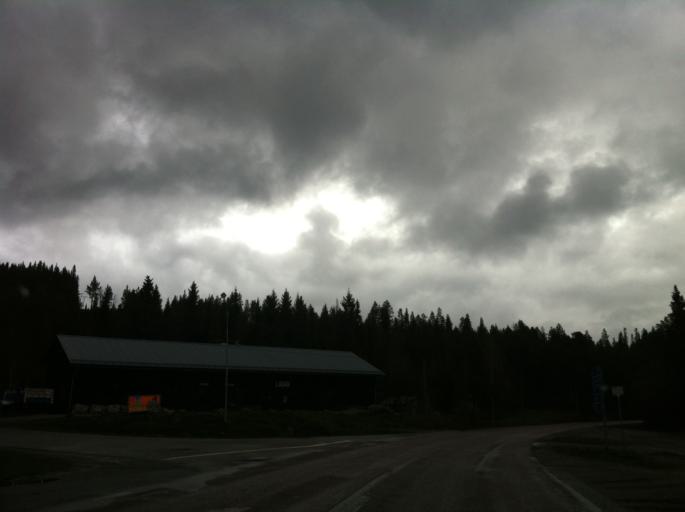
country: NO
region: Hedmark
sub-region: Engerdal
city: Engerdal
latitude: 62.4257
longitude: 12.7282
